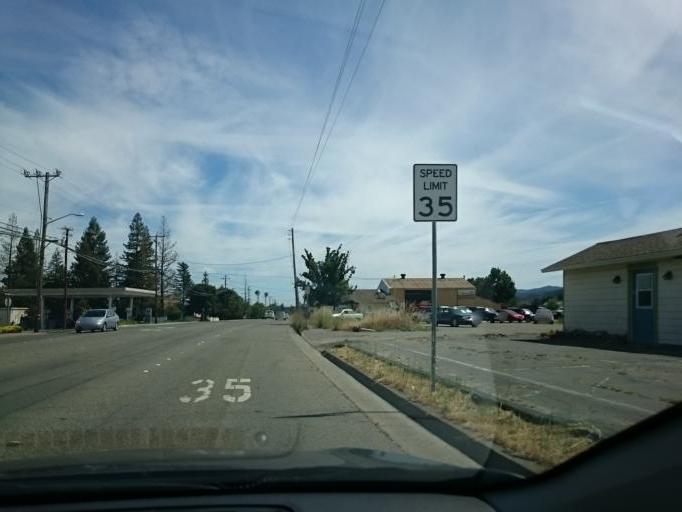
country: US
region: California
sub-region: Sonoma County
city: Healdsburg
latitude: 38.6300
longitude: -122.8727
